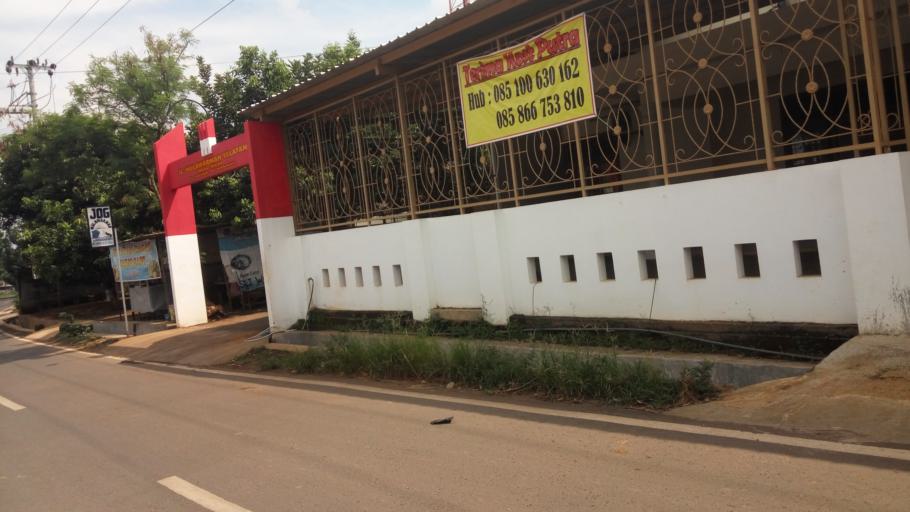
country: ID
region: Central Java
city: Ungaran
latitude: -7.0703
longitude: 110.4393
